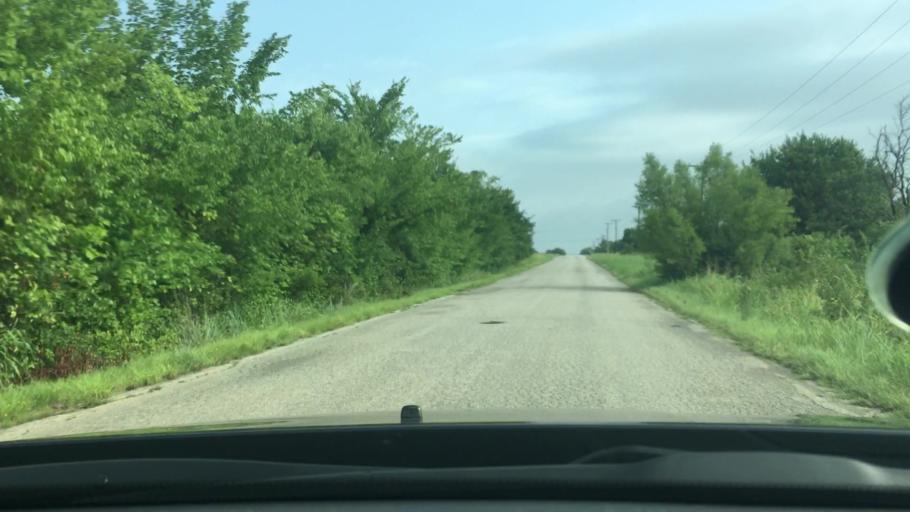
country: US
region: Oklahoma
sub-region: Carter County
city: Lone Grove
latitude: 34.2218
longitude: -97.2737
